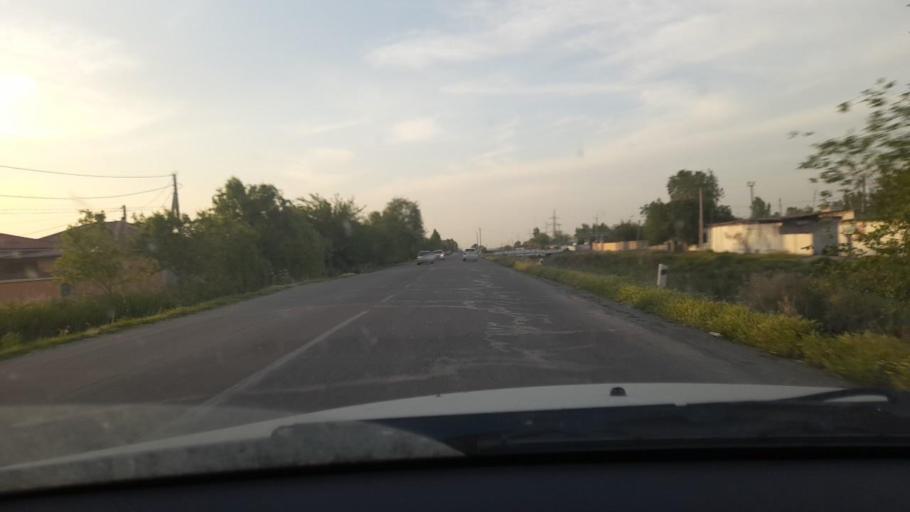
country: UZ
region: Sirdaryo
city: Guliston
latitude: 40.4907
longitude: 68.7371
